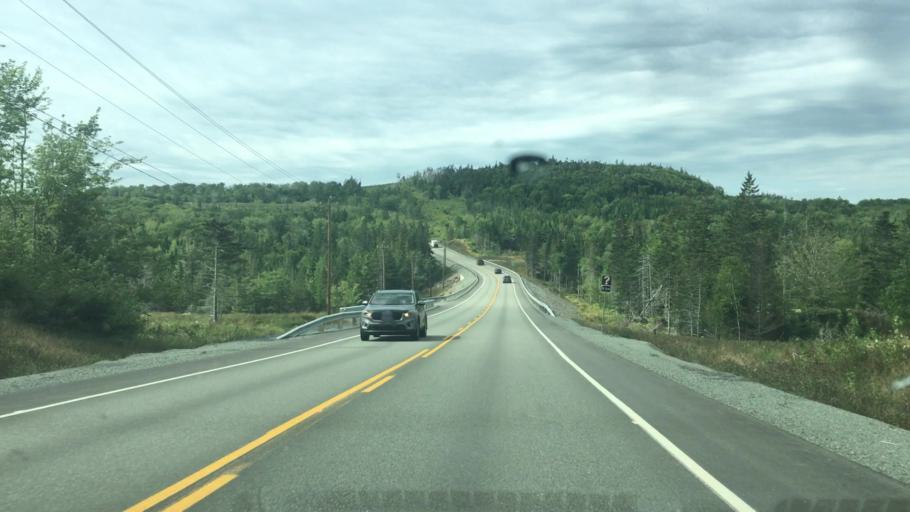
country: CA
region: Nova Scotia
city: Princeville
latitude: 45.6677
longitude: -60.8079
